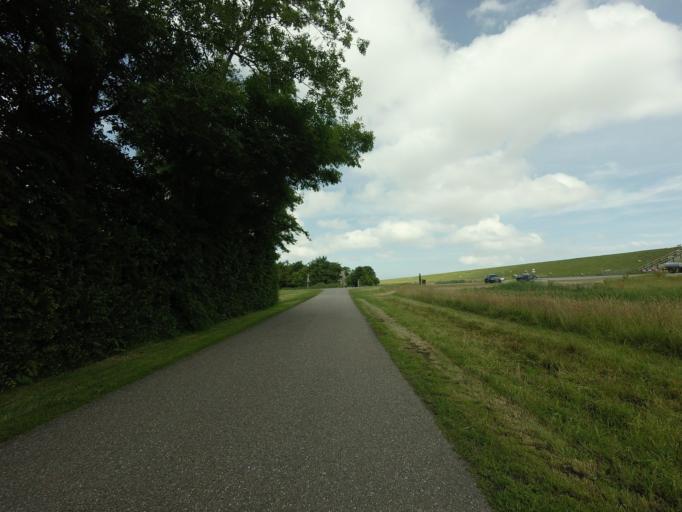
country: NL
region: North Holland
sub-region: Gemeente Texel
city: Den Burg
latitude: 53.1153
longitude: 4.8976
